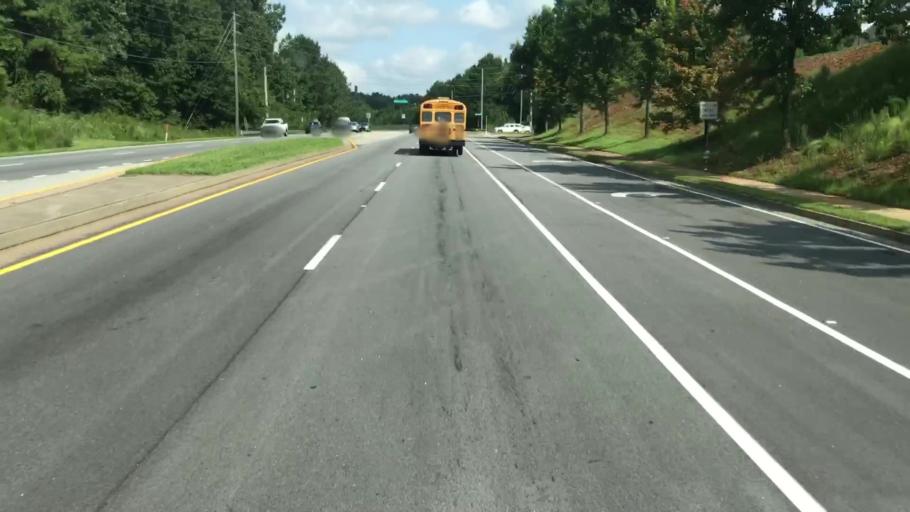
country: US
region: Georgia
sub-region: Gwinnett County
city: Lawrenceville
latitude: 33.9336
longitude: -84.0289
